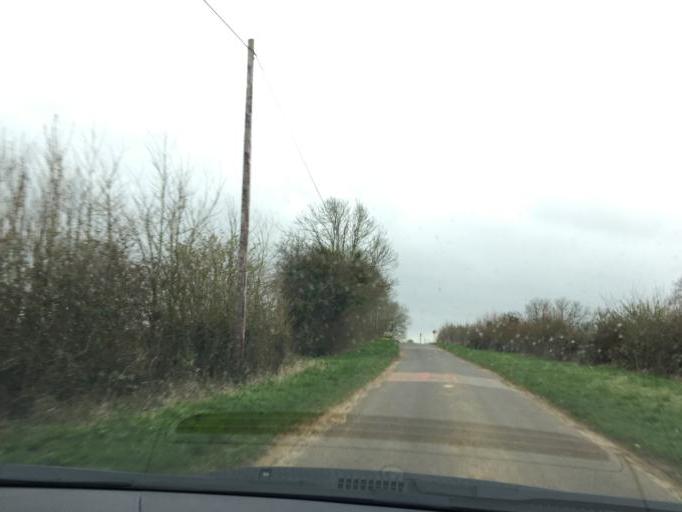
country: GB
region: England
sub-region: Oxfordshire
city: Deddington
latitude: 51.9346
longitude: -1.3707
